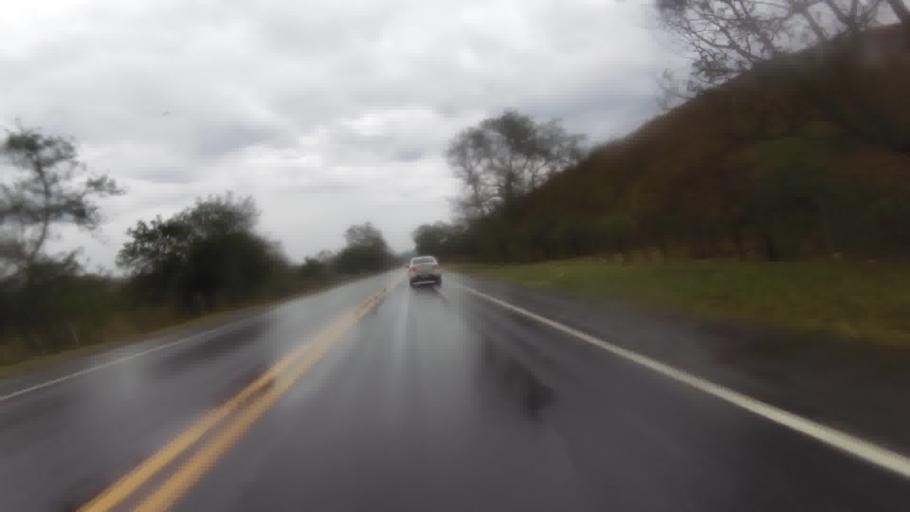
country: BR
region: Espirito Santo
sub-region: Cachoeiro De Itapemirim
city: Cachoeiro de Itapemirim
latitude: -20.9954
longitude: -41.1259
